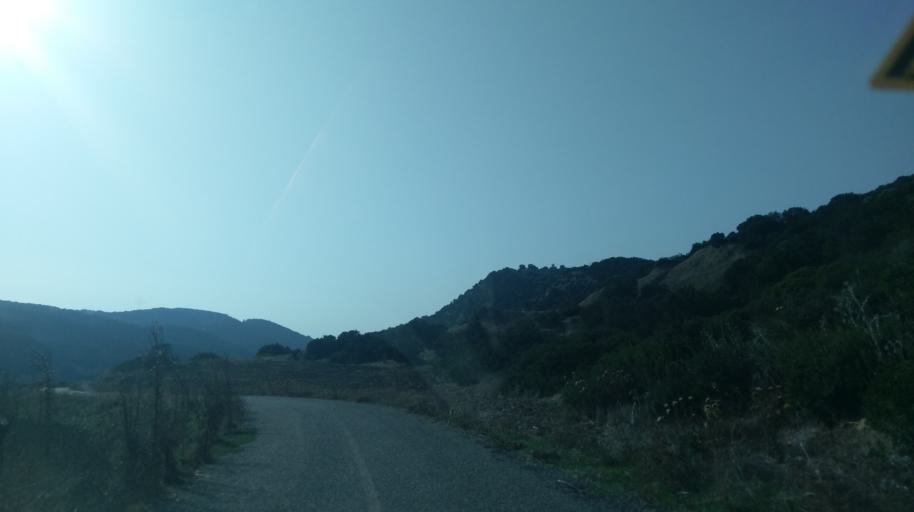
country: CY
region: Ammochostos
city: Rizokarpaso
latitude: 35.5553
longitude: 34.3693
